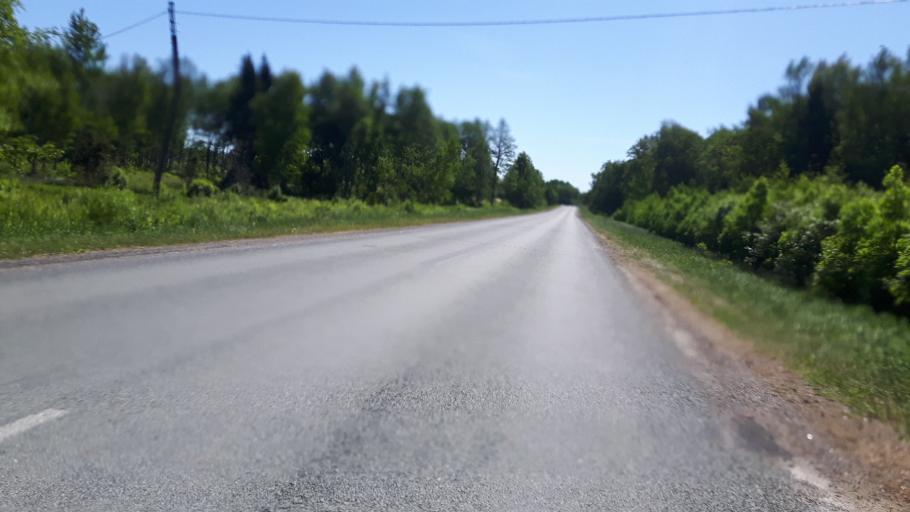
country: EE
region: Harju
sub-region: Kuusalu vald
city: Kuusalu
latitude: 59.4628
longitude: 25.4491
